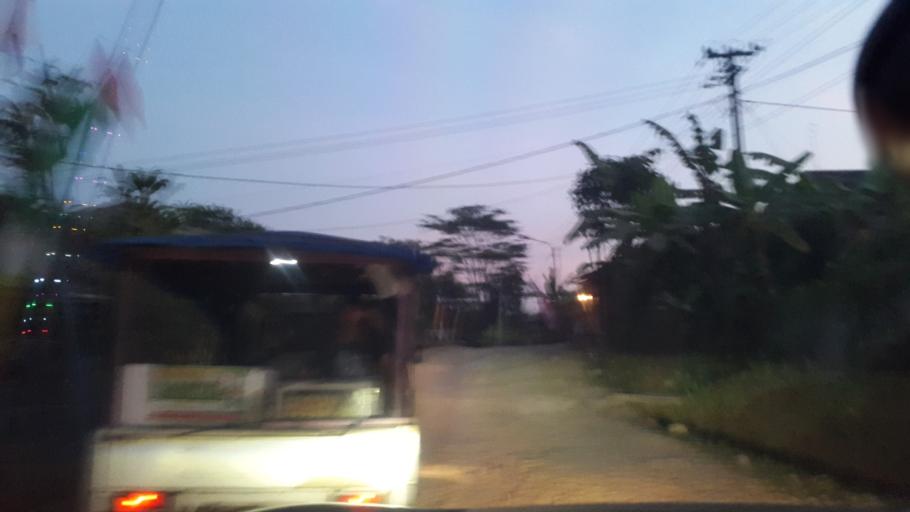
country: ID
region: West Java
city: Gunungkalong
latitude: -6.9593
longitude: 106.8367
